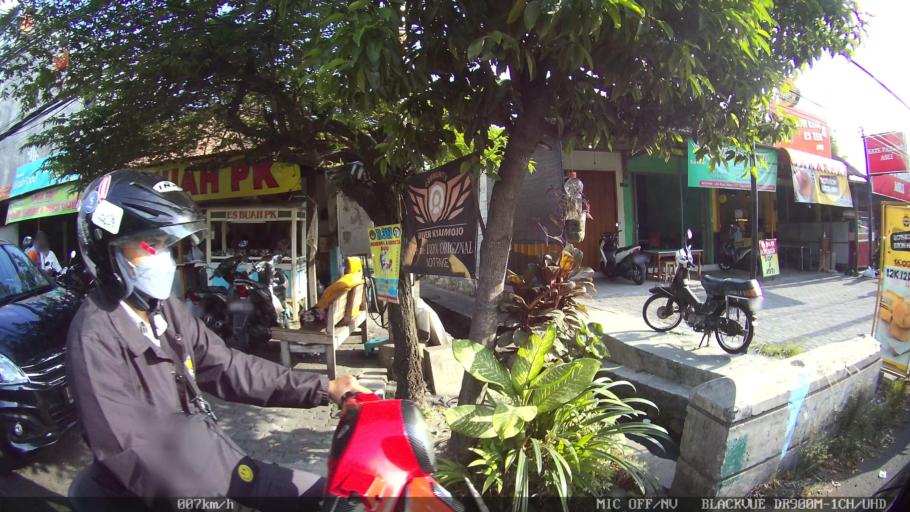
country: ID
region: Daerah Istimewa Yogyakarta
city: Yogyakarta
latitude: -7.7815
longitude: 110.3512
